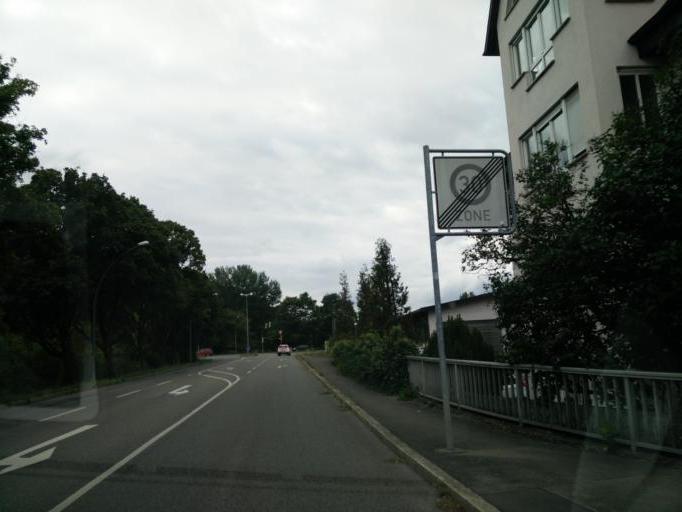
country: DE
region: Baden-Wuerttemberg
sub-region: Tuebingen Region
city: Tuebingen
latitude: 48.5271
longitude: 9.0795
